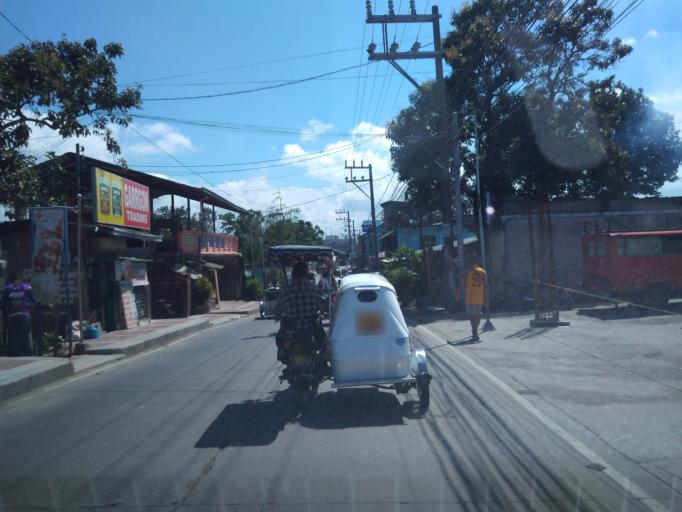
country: PH
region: Central Luzon
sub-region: Province of Bulacan
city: Bitungol
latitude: 14.8592
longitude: 121.0527
